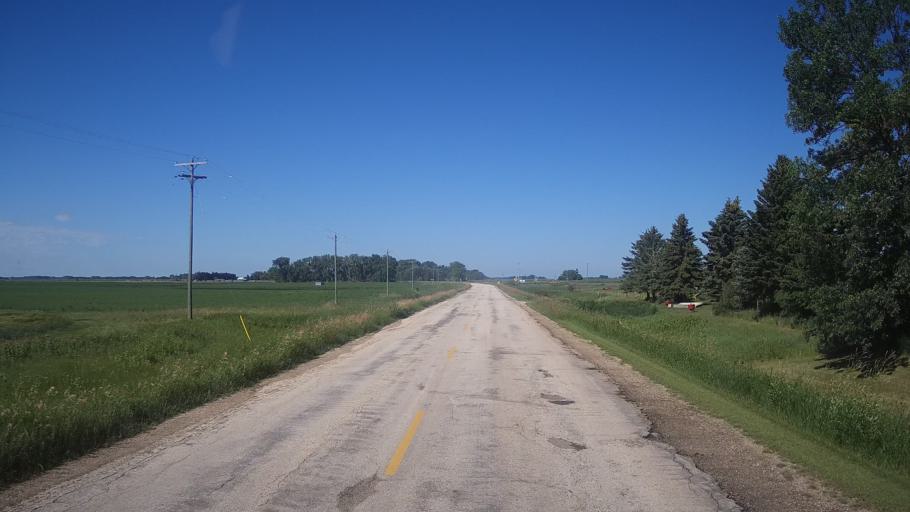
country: CA
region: Manitoba
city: Portage la Prairie
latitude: 50.0427
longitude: -98.0618
